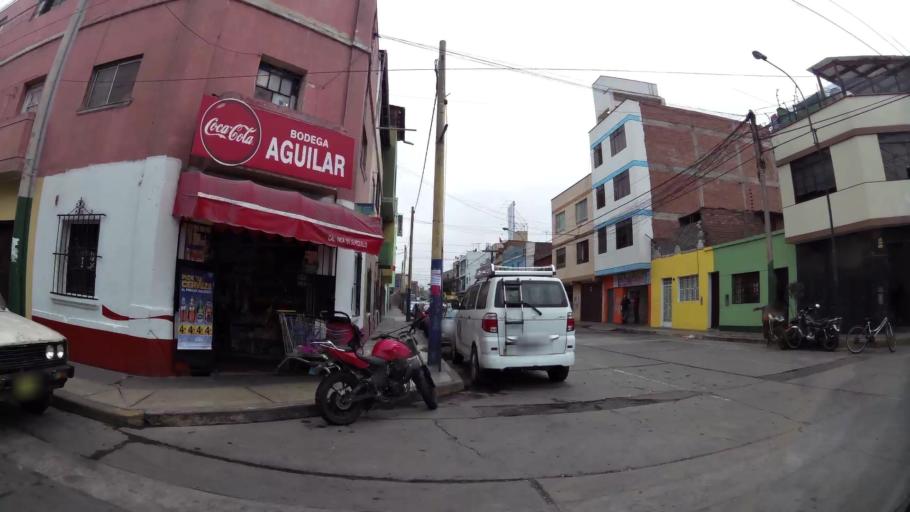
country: PE
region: Lima
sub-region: Lima
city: San Isidro
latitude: -12.1142
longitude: -77.0211
